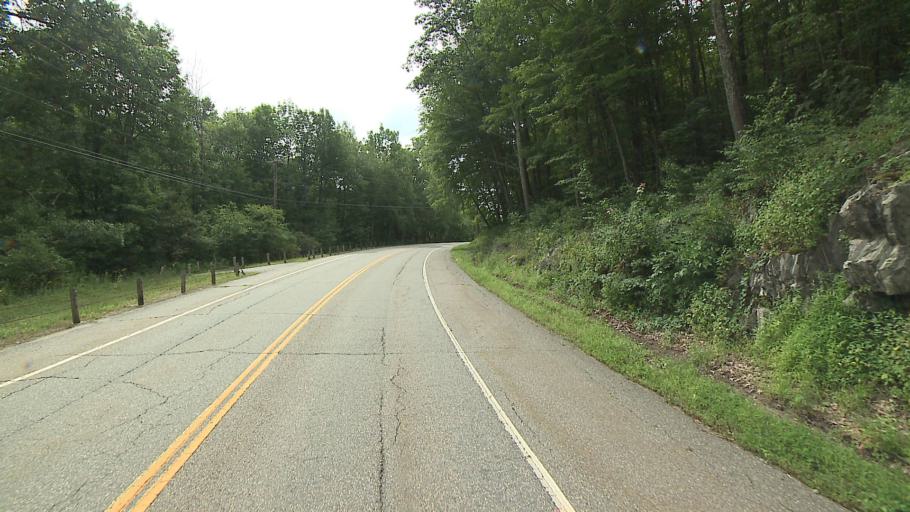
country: US
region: Connecticut
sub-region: Litchfield County
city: New Preston
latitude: 41.6753
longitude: -73.3257
